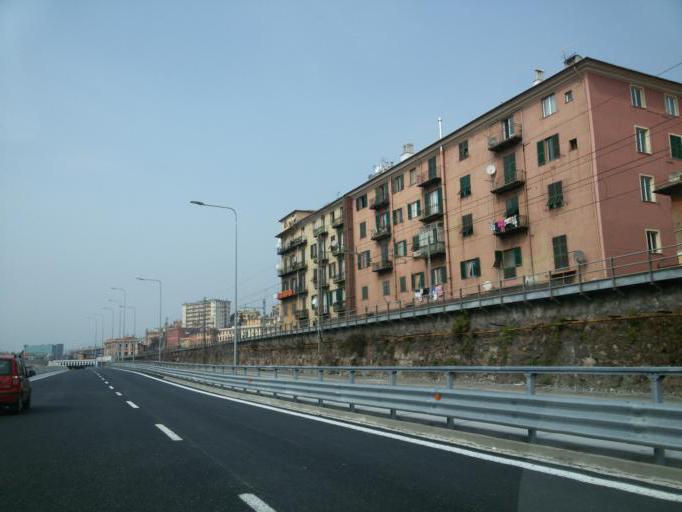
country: IT
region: Liguria
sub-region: Provincia di Genova
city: San Teodoro
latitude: 44.4137
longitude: 8.8692
